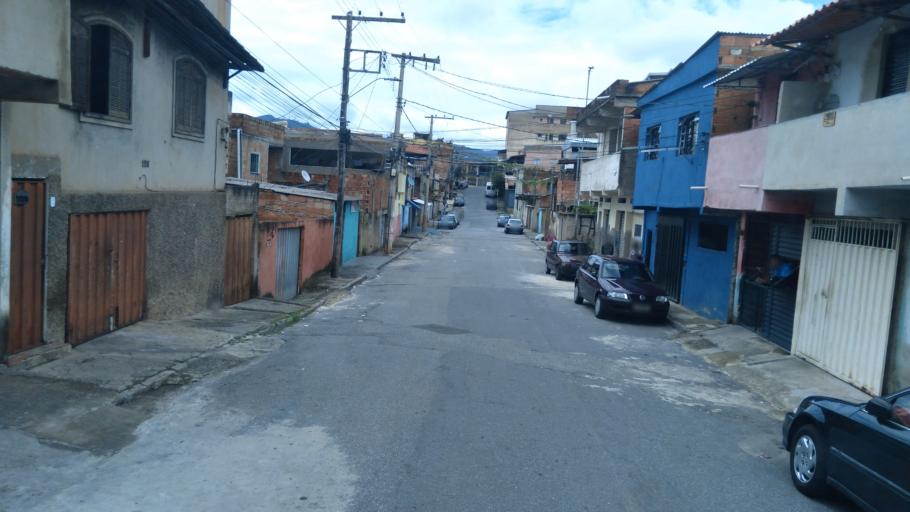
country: BR
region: Minas Gerais
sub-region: Belo Horizonte
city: Belo Horizonte
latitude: -19.8955
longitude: -43.8899
